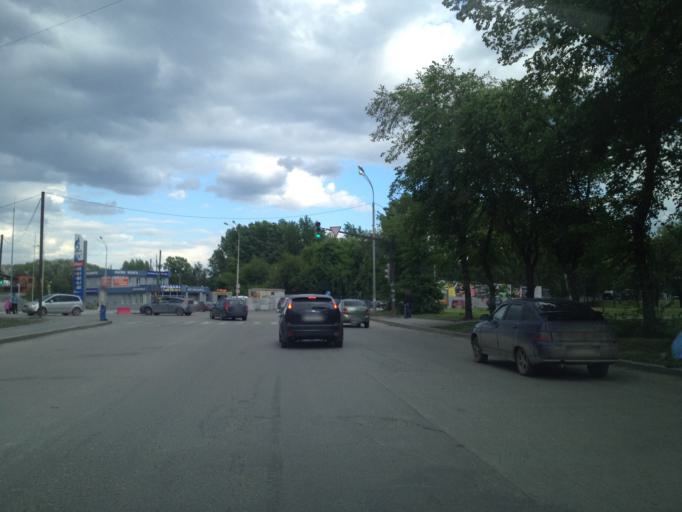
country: RU
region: Sverdlovsk
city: Yekaterinburg
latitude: 56.7986
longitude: 60.5943
